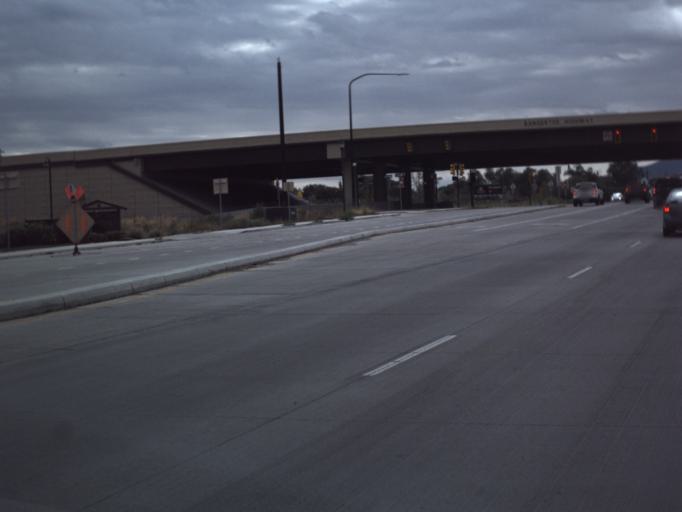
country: US
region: Utah
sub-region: Salt Lake County
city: Bluffdale
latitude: 40.5020
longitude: -111.9388
